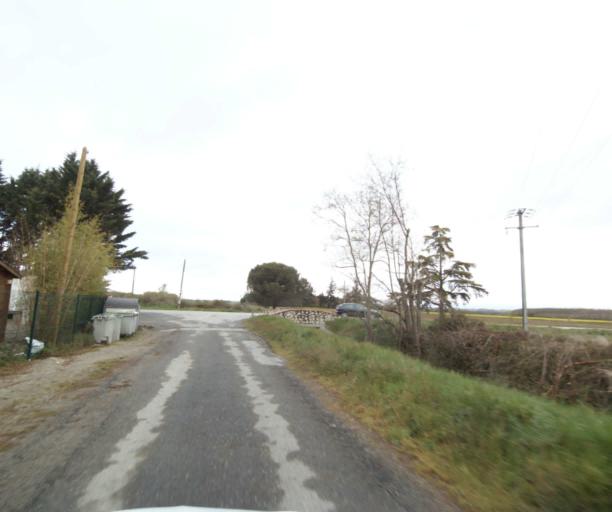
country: FR
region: Midi-Pyrenees
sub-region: Departement de l'Ariege
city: Saverdun
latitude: 43.2294
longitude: 1.6144
